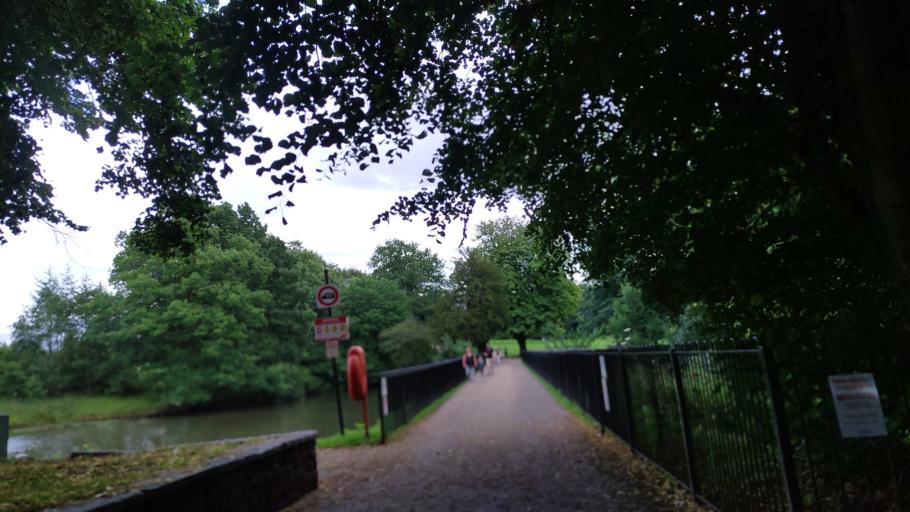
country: GB
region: England
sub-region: Lancashire
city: Chorley
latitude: 53.6588
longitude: -2.6456
